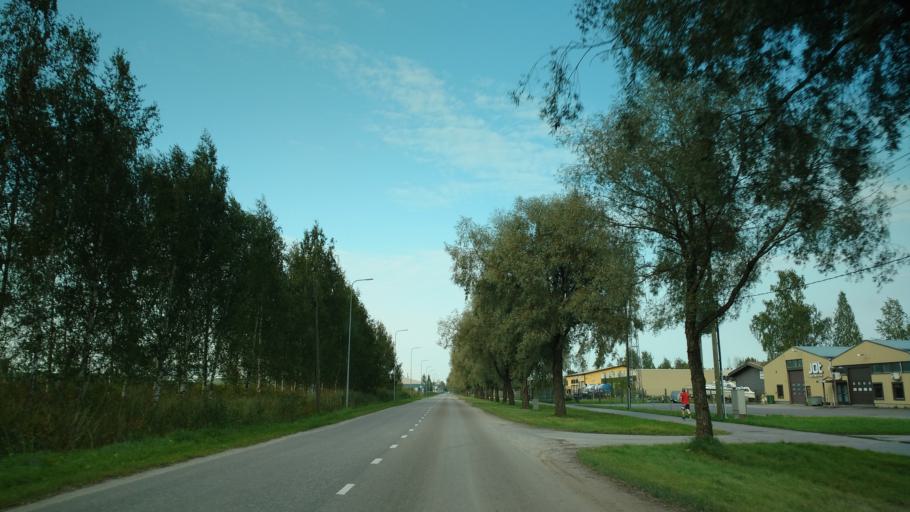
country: FI
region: Varsinais-Suomi
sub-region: Salo
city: Salo
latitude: 60.3710
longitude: 23.1016
